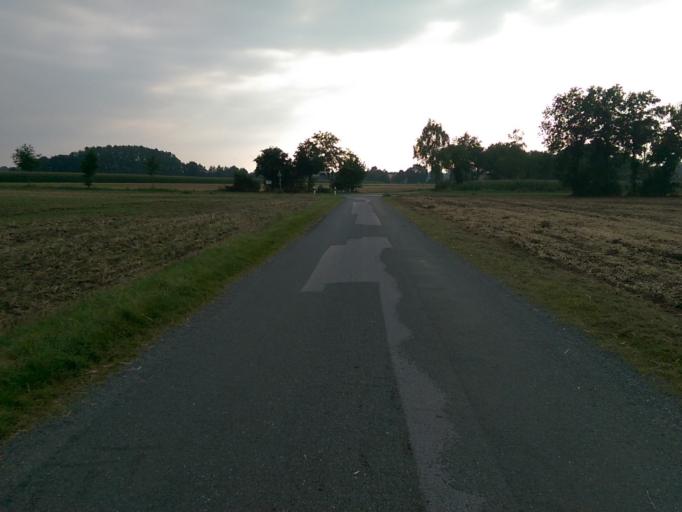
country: DE
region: North Rhine-Westphalia
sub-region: Regierungsbezirk Detmold
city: Rheda-Wiedenbruck
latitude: 51.8893
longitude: 8.3002
